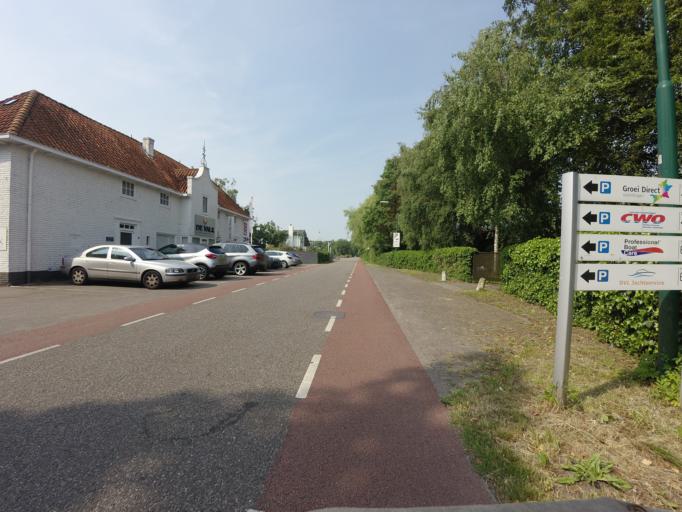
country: NL
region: North Holland
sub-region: Gemeente Wijdemeren
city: Oud-Loosdrecht
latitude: 52.1838
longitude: 5.0687
